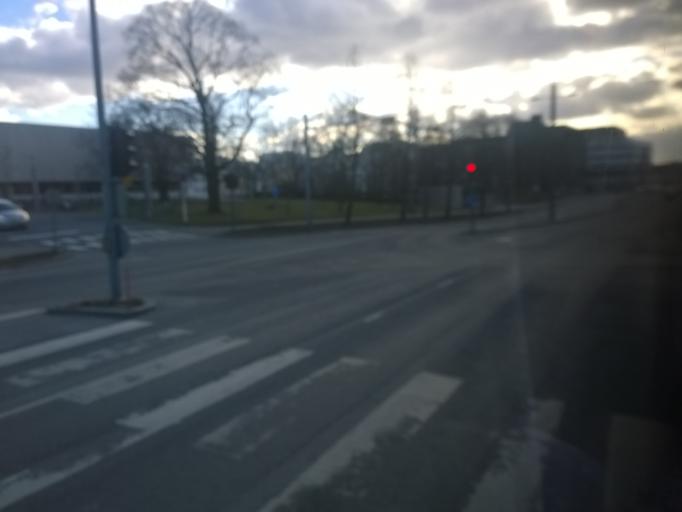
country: FI
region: Pirkanmaa
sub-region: Tampere
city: Tampere
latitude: 61.4950
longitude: 23.7802
